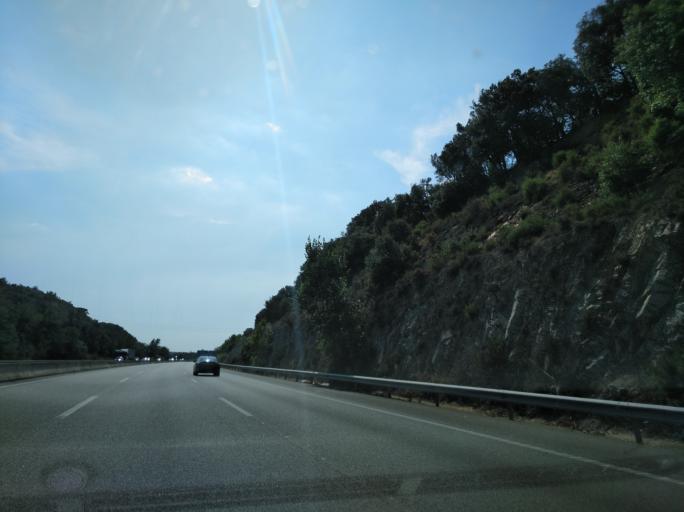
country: ES
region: Catalonia
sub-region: Provincia de Barcelona
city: Sant Celoni
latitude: 41.6853
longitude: 2.4983
